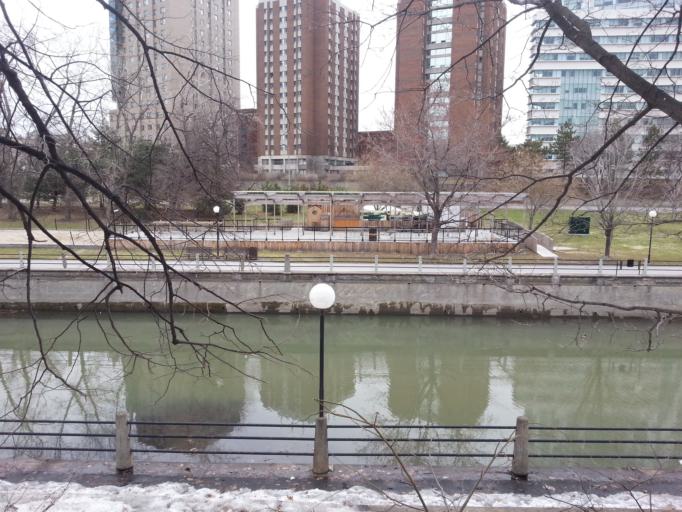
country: CA
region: Ontario
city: Ottawa
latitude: 45.4208
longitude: -75.6858
